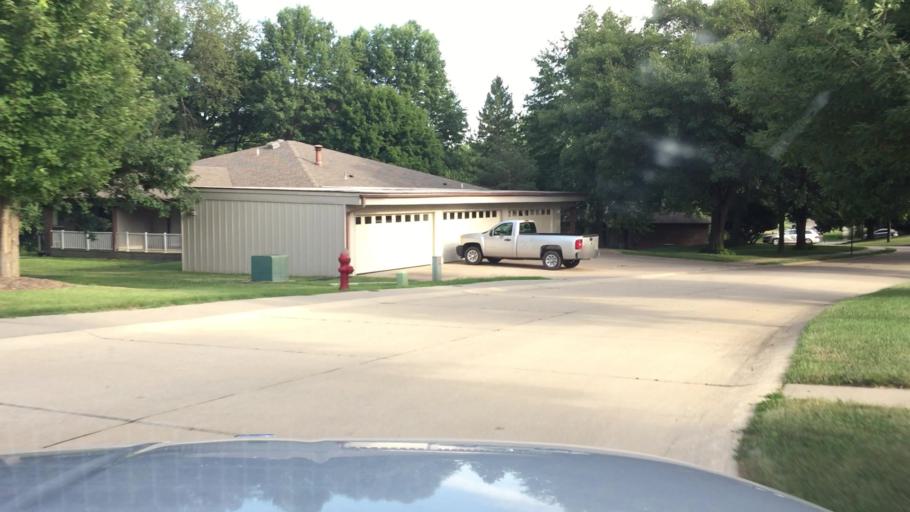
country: US
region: Iowa
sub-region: Johnson County
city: Iowa City
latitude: 41.6618
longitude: -91.4932
